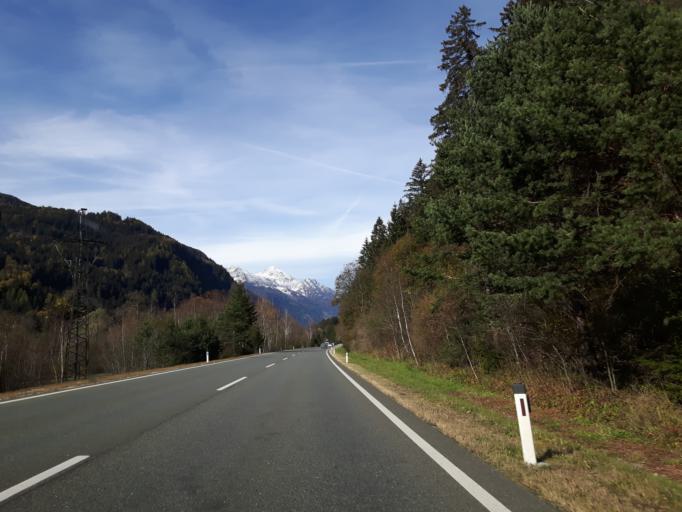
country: AT
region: Tyrol
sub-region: Politischer Bezirk Lienz
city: Schlaiten
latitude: 46.8818
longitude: 12.6640
